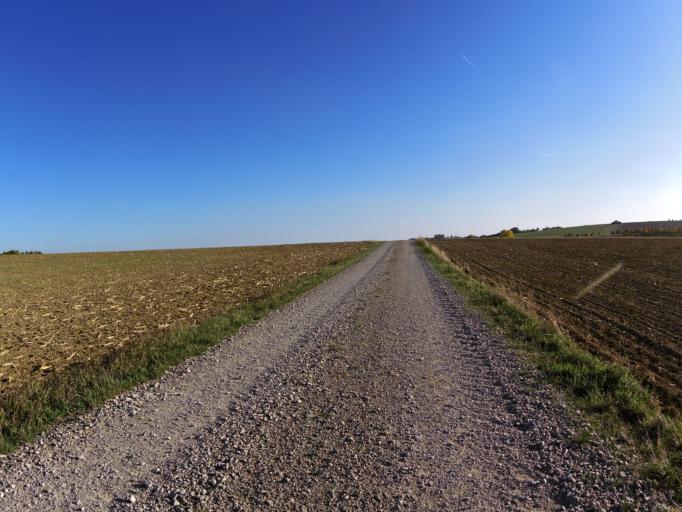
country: DE
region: Bavaria
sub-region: Regierungsbezirk Unterfranken
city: Reichenberg
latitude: 49.7201
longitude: 9.9236
